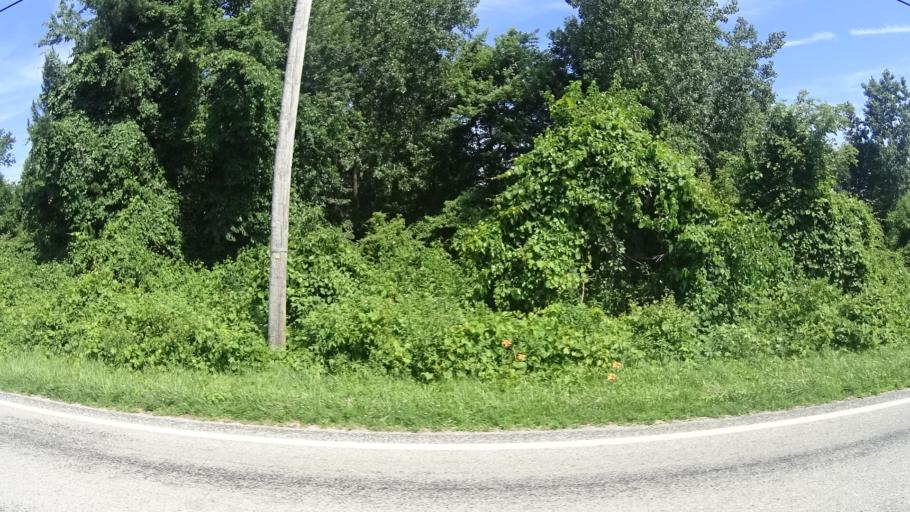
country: US
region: Ohio
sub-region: Erie County
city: Huron
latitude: 41.3401
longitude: -82.4676
